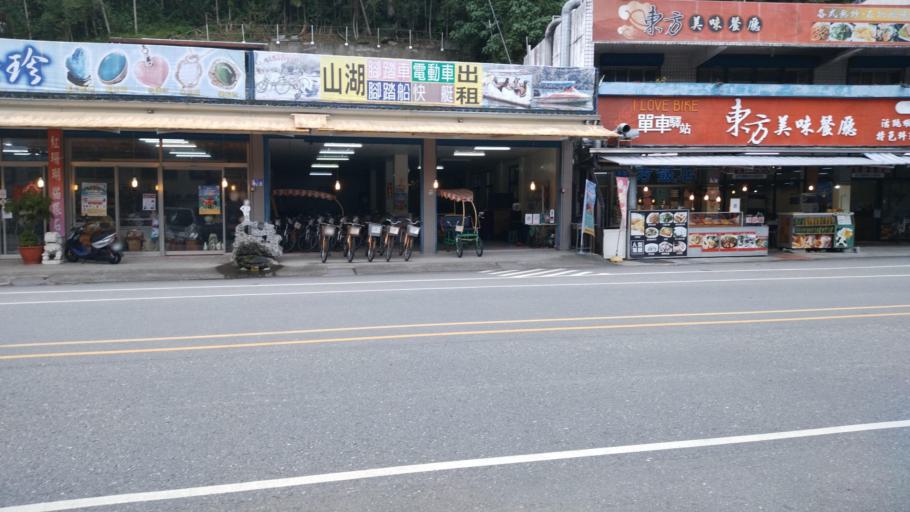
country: TW
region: Taiwan
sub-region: Hualien
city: Hualian
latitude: 23.9271
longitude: 121.5055
